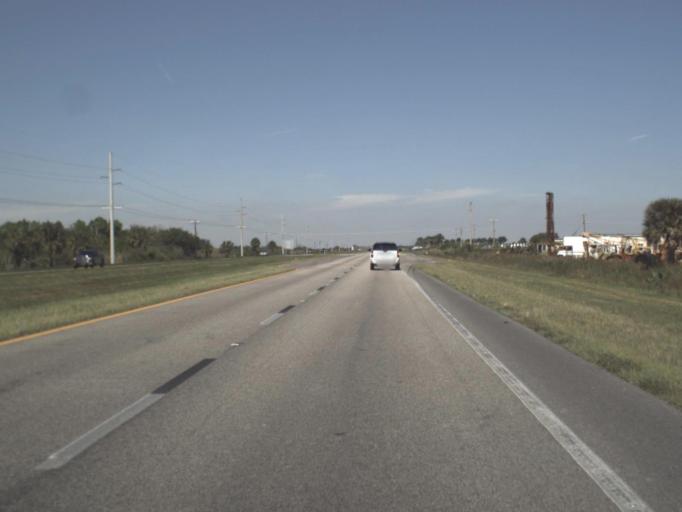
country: US
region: Florida
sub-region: Glades County
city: Moore Haven
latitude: 26.7714
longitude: -81.0828
